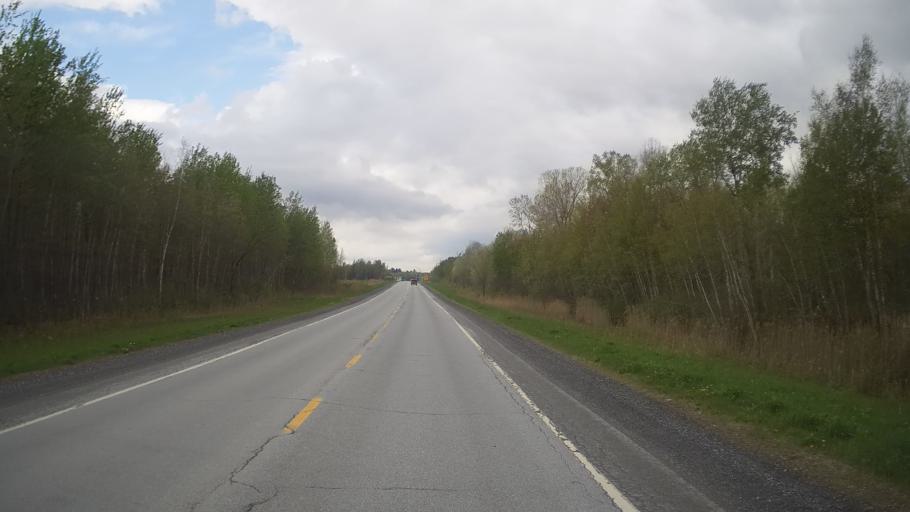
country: CA
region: Quebec
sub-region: Monteregie
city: Farnham
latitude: 45.2726
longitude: -72.9736
